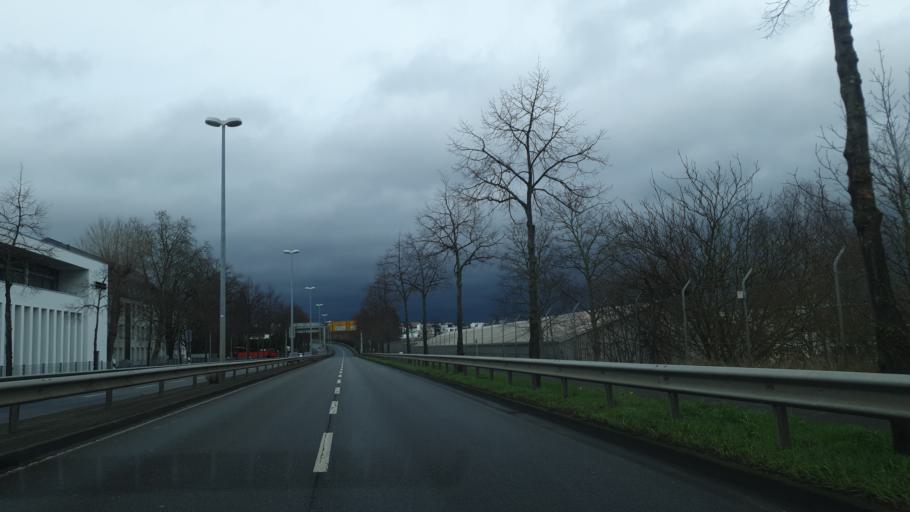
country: DE
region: Rheinland-Pfalz
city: Koblenz
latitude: 50.3631
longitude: 7.5601
